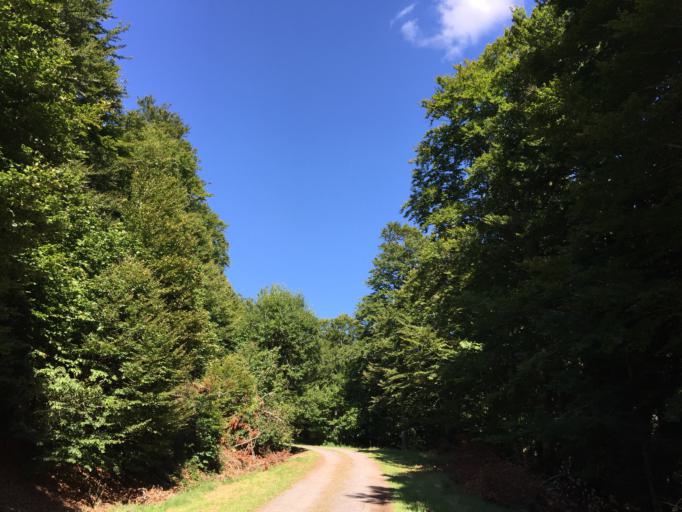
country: FR
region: Midi-Pyrenees
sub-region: Departement de l'Aveyron
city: Laguiole
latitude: 44.6416
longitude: 2.9273
